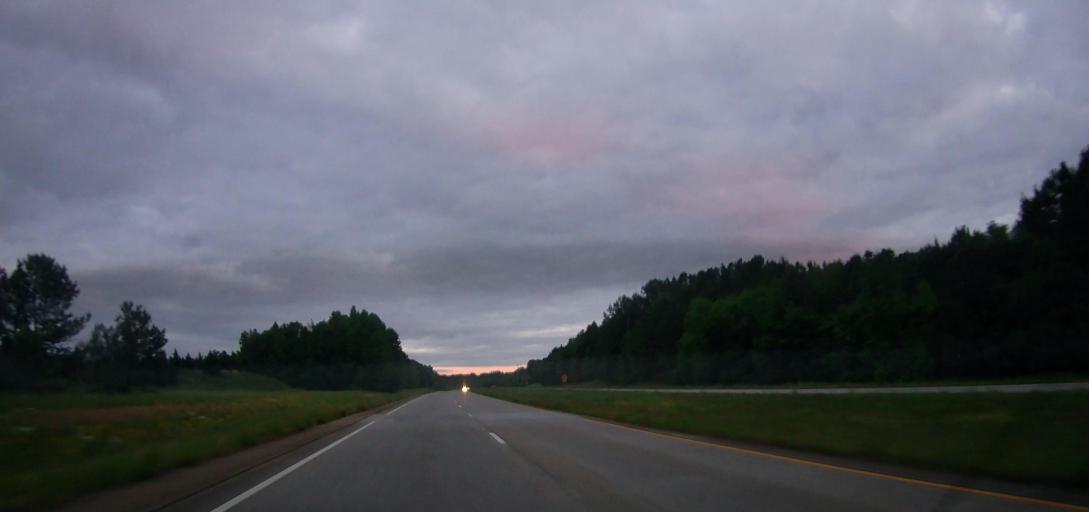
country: US
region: Georgia
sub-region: Jackson County
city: Arcade
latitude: 34.0840
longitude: -83.5780
